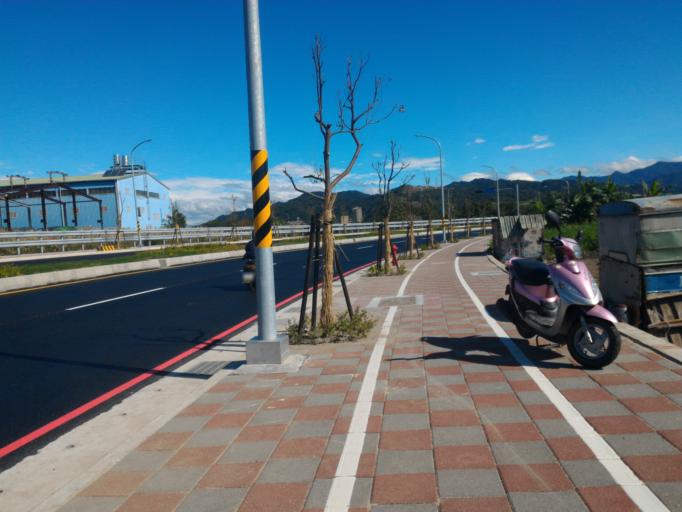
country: TW
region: Taiwan
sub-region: Taoyuan
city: Taoyuan
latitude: 24.9399
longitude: 121.3854
